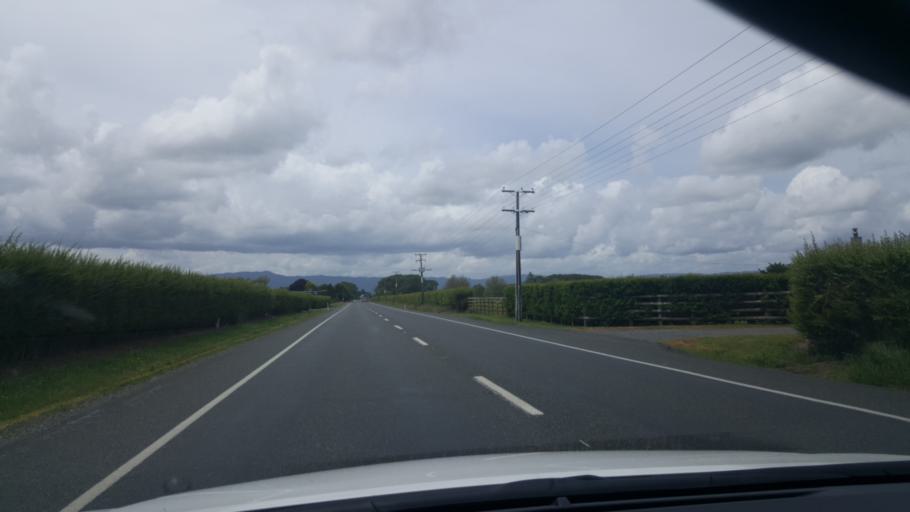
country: NZ
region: Waikato
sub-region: Matamata-Piako District
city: Matamata
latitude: -37.8821
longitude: 175.7390
